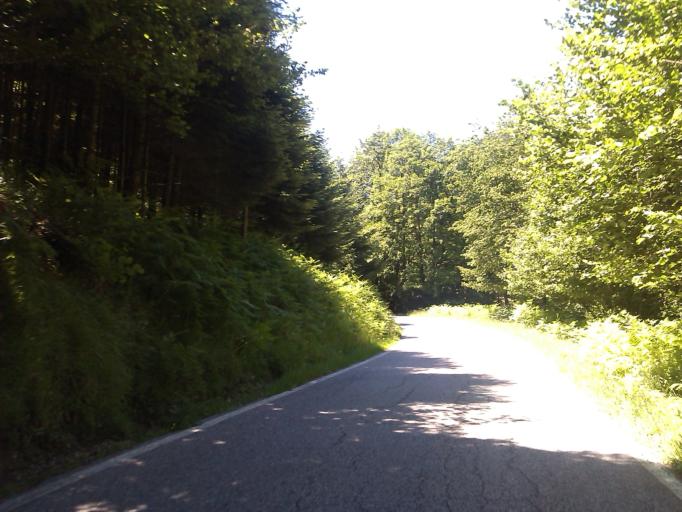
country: IT
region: Tuscany
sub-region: Provincia di Prato
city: Cantagallo
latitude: 44.0316
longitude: 11.0396
